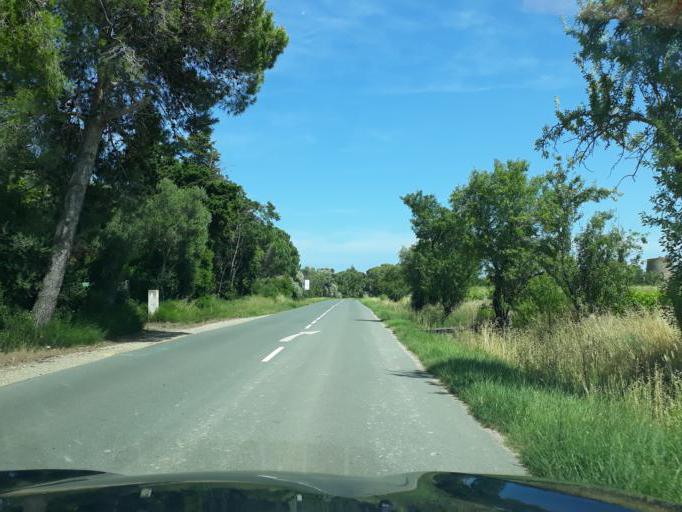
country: FR
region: Languedoc-Roussillon
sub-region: Departement de l'Aude
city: Portel-des-Corbieres
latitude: 43.0395
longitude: 2.9435
